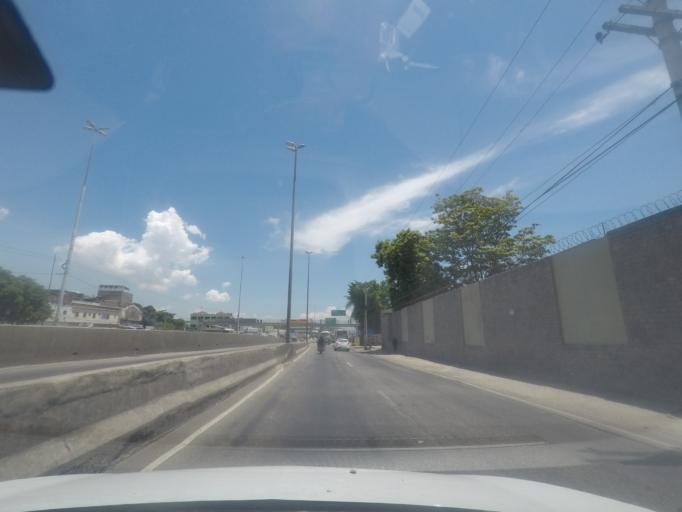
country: BR
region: Rio de Janeiro
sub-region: Rio De Janeiro
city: Rio de Janeiro
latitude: -22.8655
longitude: -43.2476
